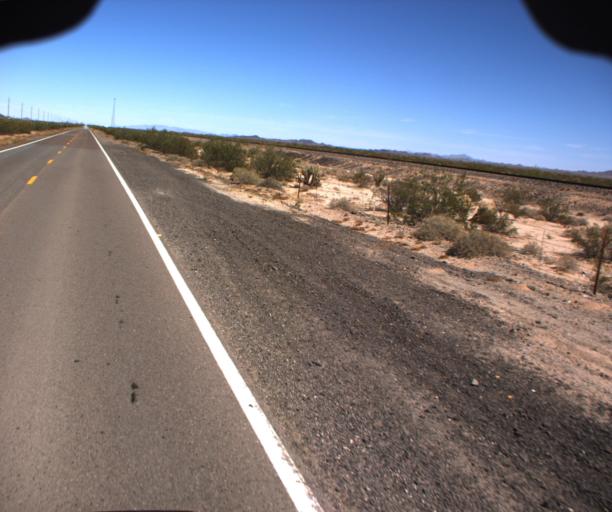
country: US
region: Arizona
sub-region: La Paz County
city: Salome
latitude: 33.8285
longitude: -113.8730
